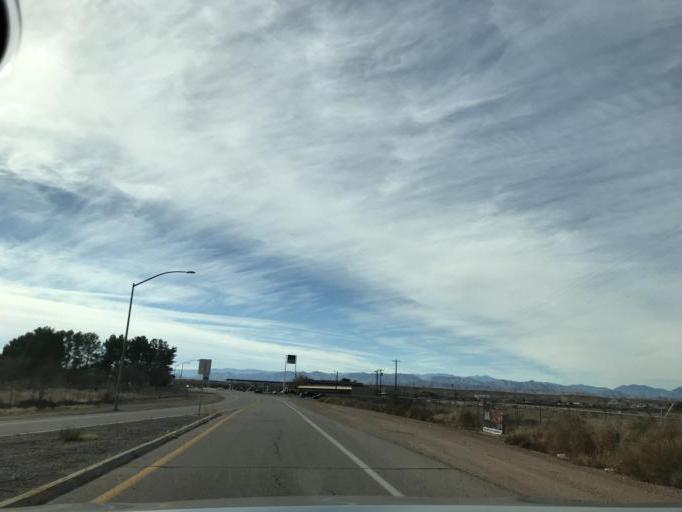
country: US
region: Nevada
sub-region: Clark County
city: Moapa Town
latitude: 36.6662
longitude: -114.5662
